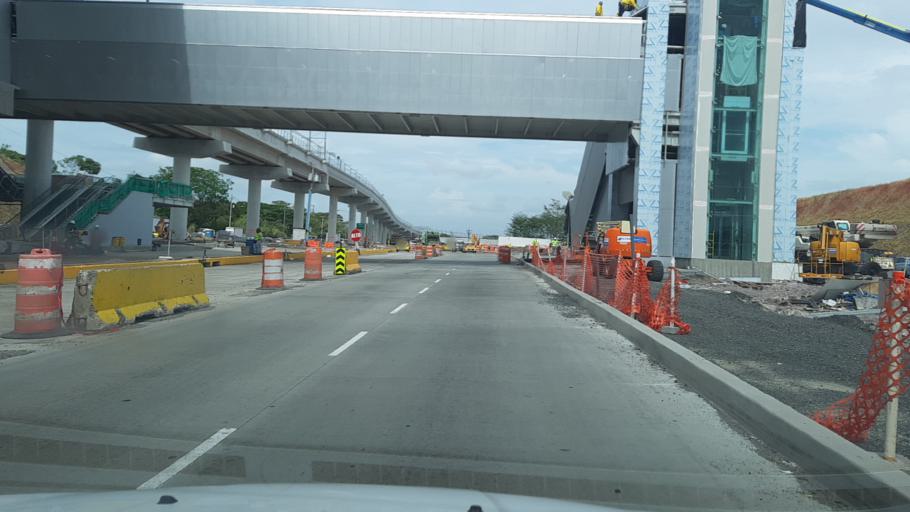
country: PA
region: Panama
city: Cabra Numero Uno
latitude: 9.1016
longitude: -79.3534
